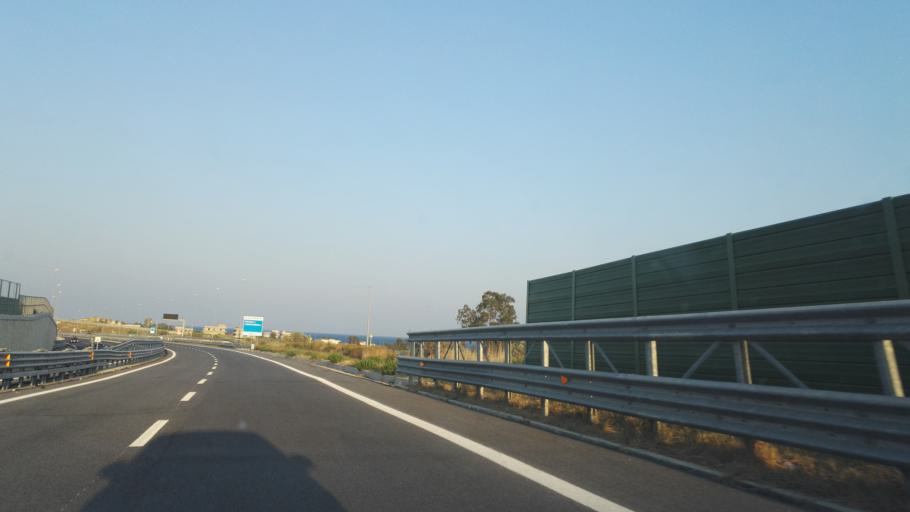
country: IT
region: Calabria
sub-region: Provincia di Reggio Calabria
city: Marina di Gioiosa Ionica
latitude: 38.3105
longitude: 16.3478
